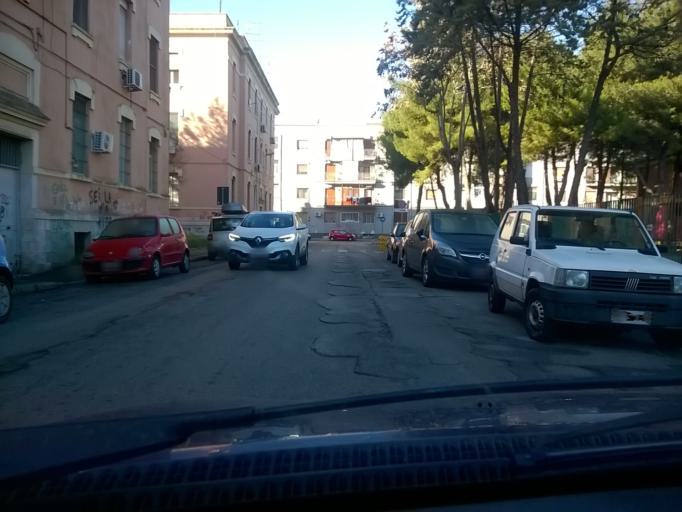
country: IT
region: Apulia
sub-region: Provincia di Taranto
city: Taranto
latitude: 40.4666
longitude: 17.2680
